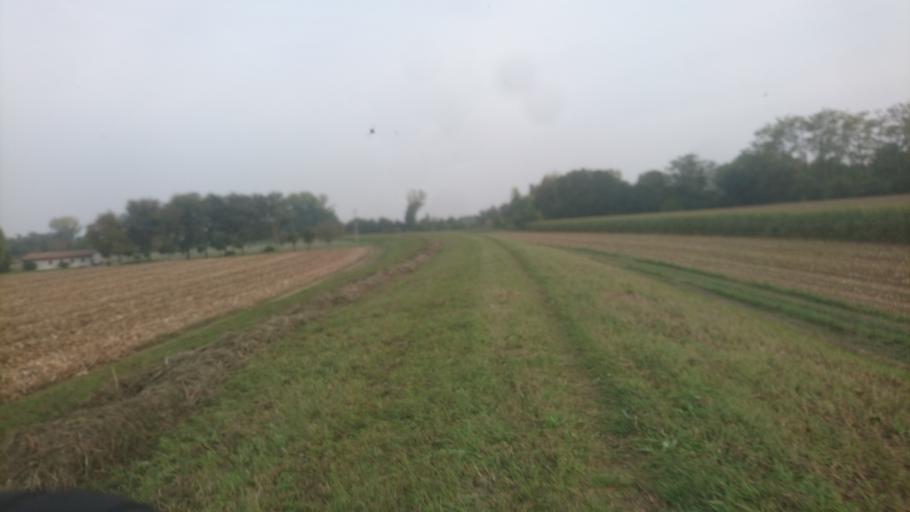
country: IT
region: Veneto
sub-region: Provincia di Padova
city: Cervarese Santa Croce
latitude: 45.4159
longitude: 11.7184
